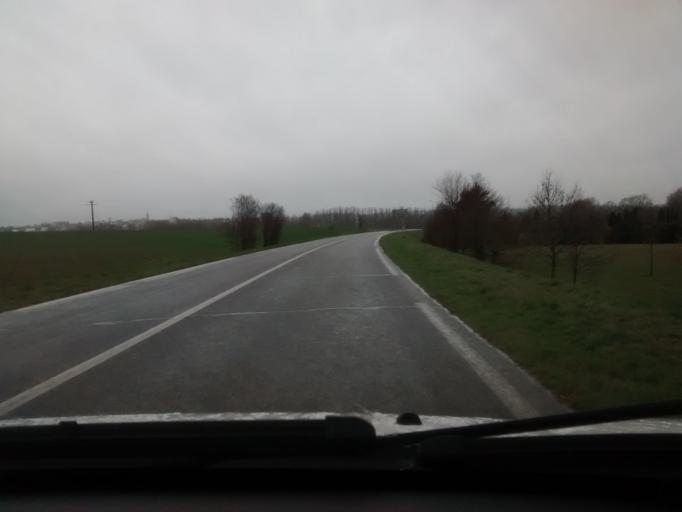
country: FR
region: Brittany
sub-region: Departement d'Ille-et-Vilaine
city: Acigne
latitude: 48.1341
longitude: -1.5178
